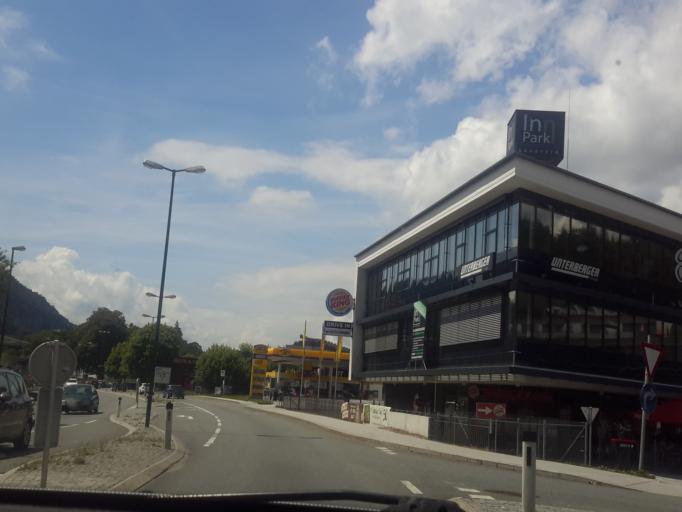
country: AT
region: Tyrol
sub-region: Politischer Bezirk Kufstein
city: Kufstein
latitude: 47.5755
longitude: 12.1590
